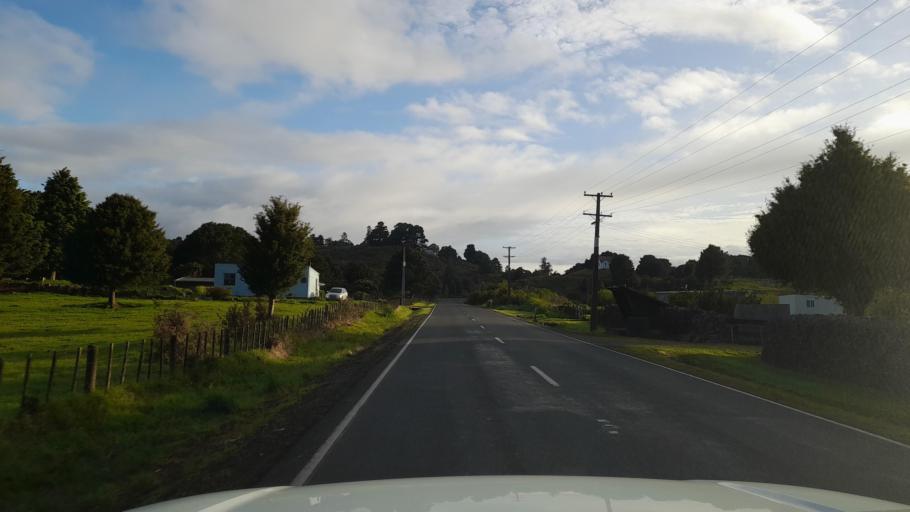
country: NZ
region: Northland
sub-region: Far North District
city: Waimate North
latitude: -35.4818
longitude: 173.8358
